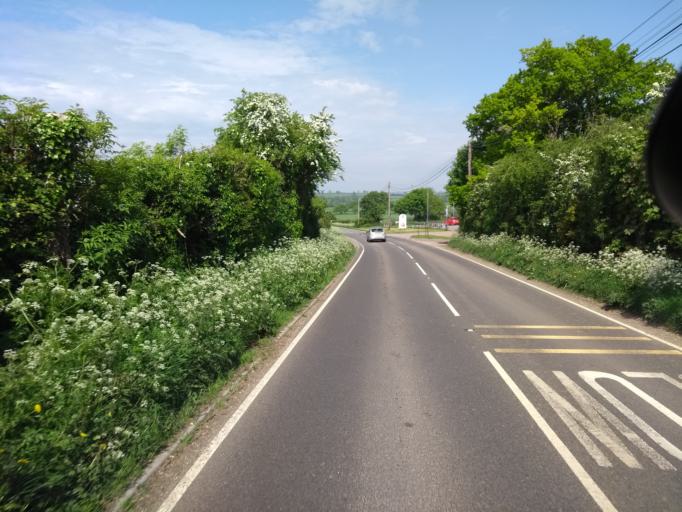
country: GB
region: England
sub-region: Somerset
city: Chard
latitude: 50.8769
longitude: -2.9874
